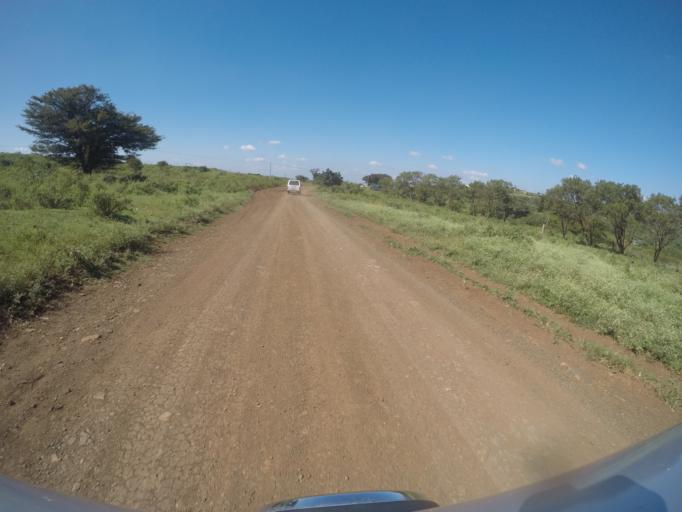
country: ZA
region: KwaZulu-Natal
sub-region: uThungulu District Municipality
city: Empangeni
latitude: -28.5633
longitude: 31.7021
